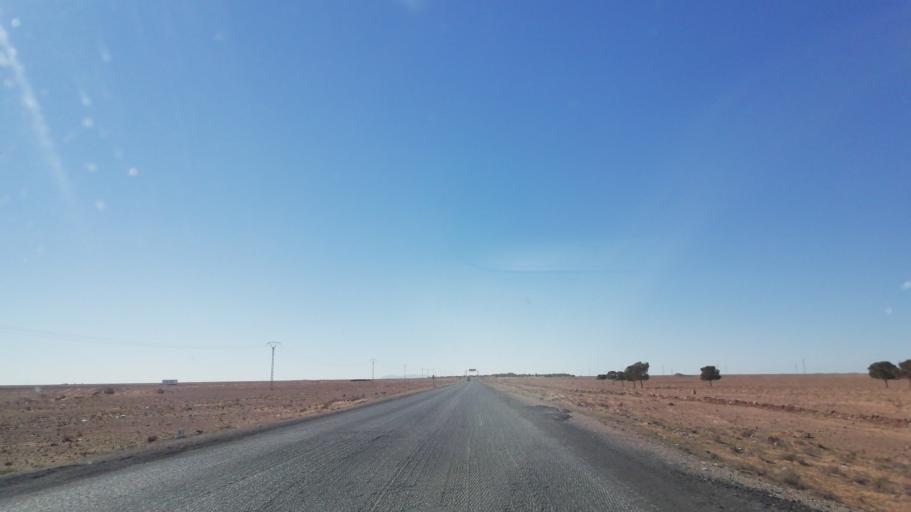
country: DZ
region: Saida
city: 'Ain el Hadjar
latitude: 34.0114
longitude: 0.0542
